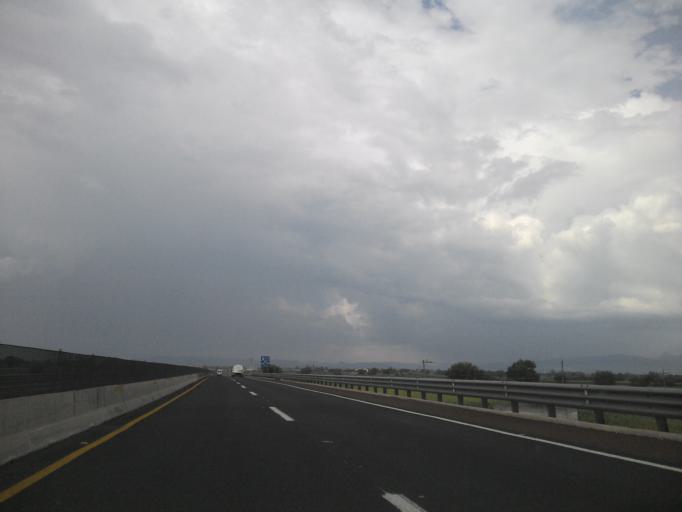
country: MX
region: Hidalgo
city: El Llano
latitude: 20.0897
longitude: -99.3127
